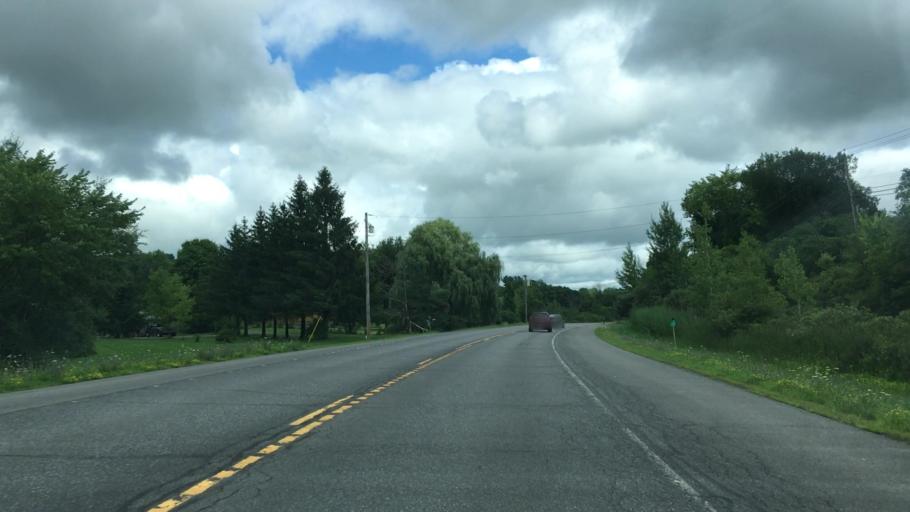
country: US
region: New York
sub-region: Rensselaer County
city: Poestenkill
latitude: 42.8013
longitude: -73.5625
